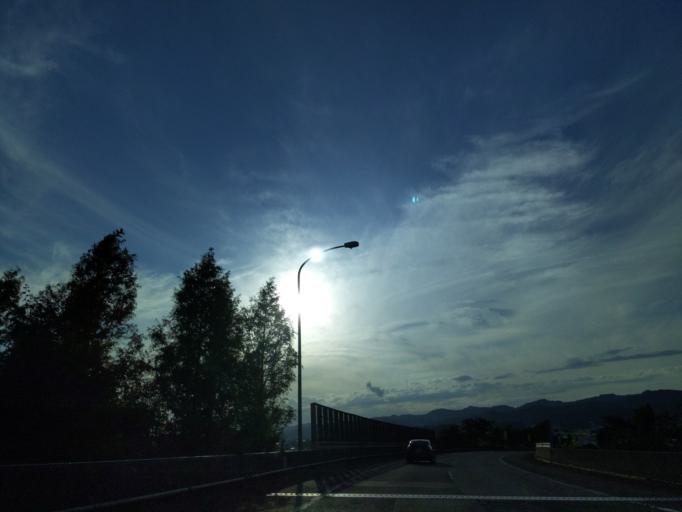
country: JP
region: Niigata
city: Nagaoka
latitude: 37.4607
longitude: 138.7919
